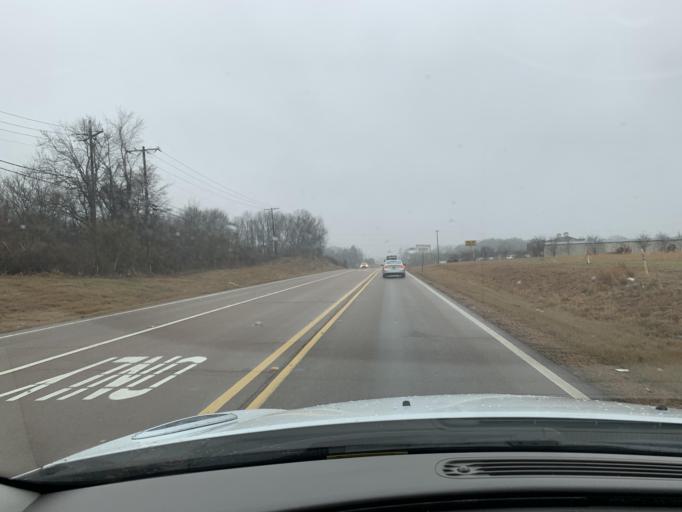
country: US
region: Mississippi
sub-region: De Soto County
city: Horn Lake
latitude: 34.9036
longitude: -89.9974
